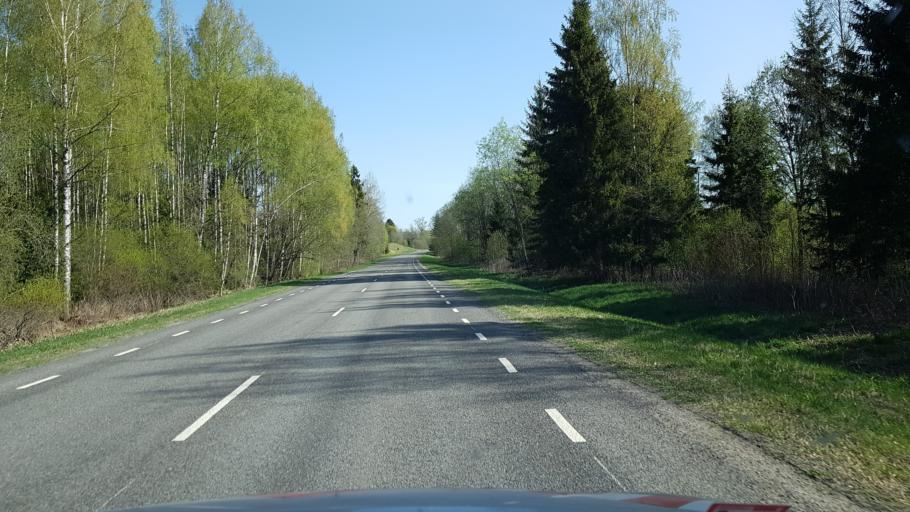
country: EE
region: Viljandimaa
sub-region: Karksi vald
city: Karksi-Nuia
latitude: 58.2315
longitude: 25.5803
